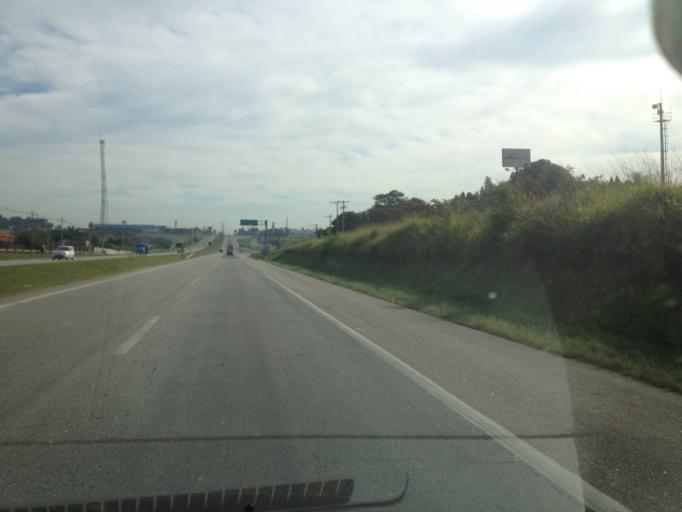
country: BR
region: Sao Paulo
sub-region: Itu
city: Itu
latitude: -23.3208
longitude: -47.3276
